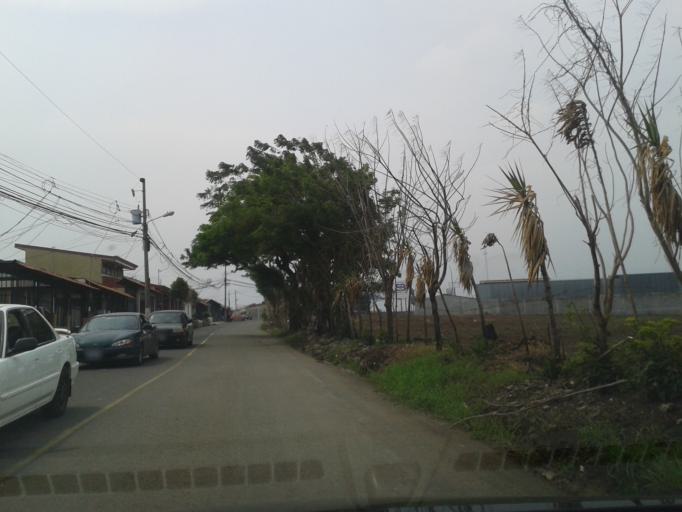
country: CR
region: Heredia
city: San Francisco
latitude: 9.9923
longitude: -84.1346
